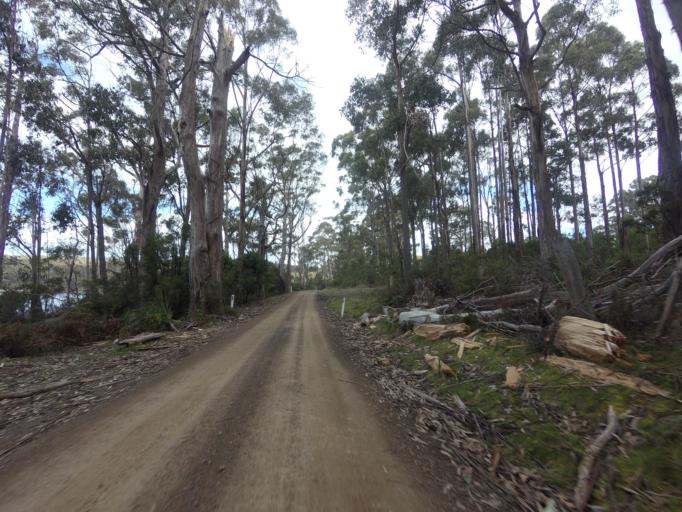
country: AU
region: Tasmania
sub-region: Huon Valley
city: Geeveston
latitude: -43.4197
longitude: 147.0140
